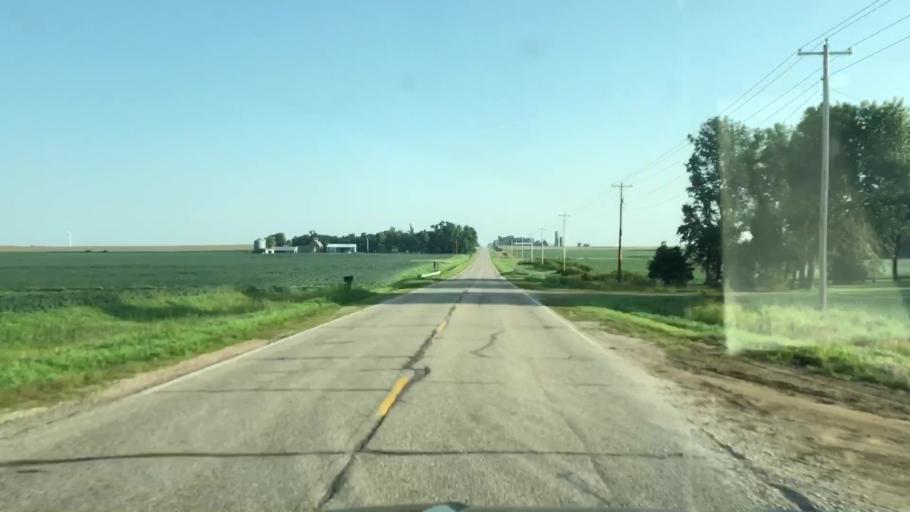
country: US
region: Iowa
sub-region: Lyon County
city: George
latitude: 43.3603
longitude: -95.9983
